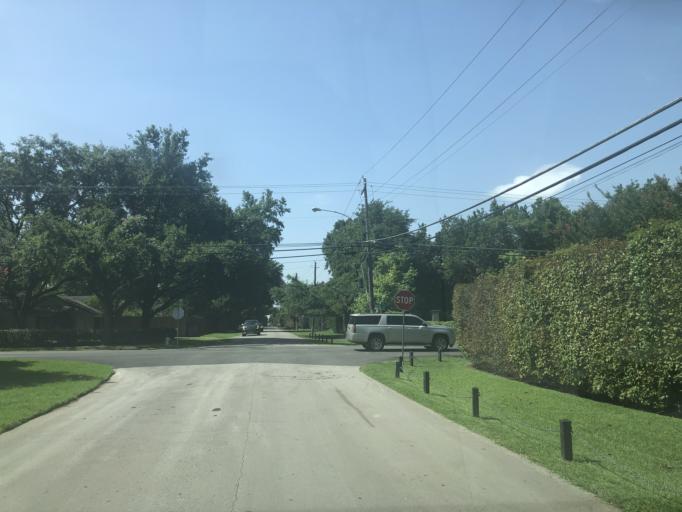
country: US
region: Texas
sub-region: Dallas County
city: University Park
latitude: 32.8742
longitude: -96.8138
